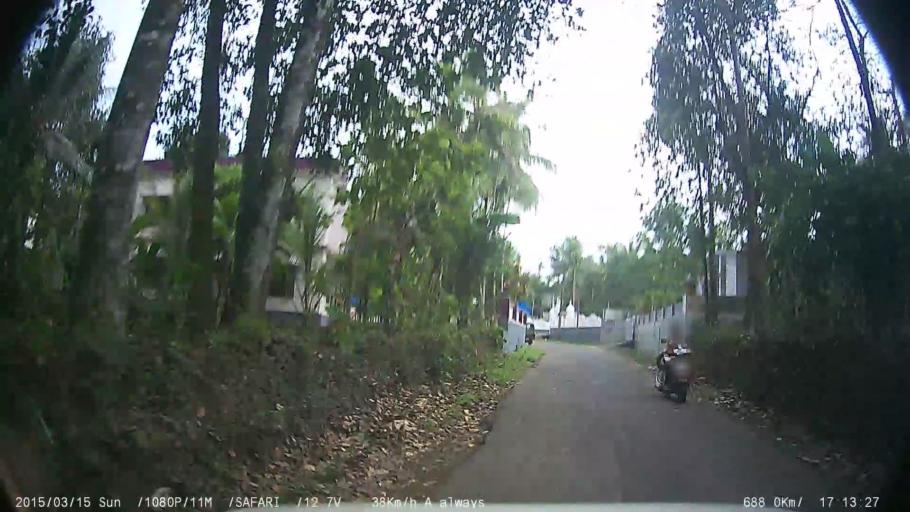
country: IN
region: Kerala
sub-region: Kottayam
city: Palackattumala
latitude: 9.8534
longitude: 76.6843
